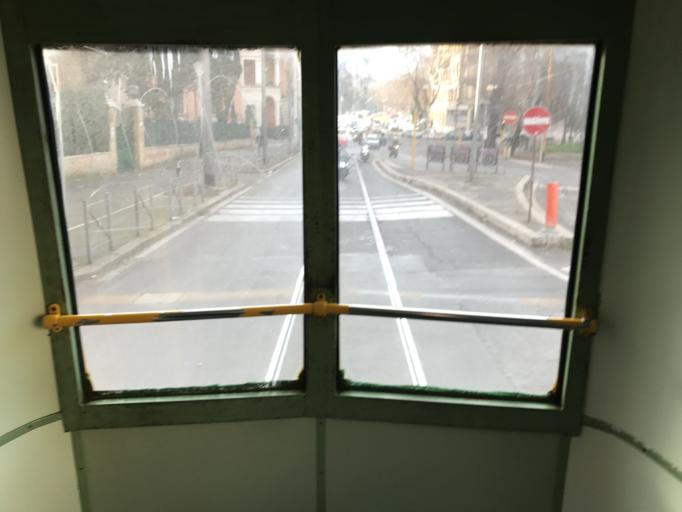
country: VA
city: Vatican City
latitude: 41.9189
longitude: 12.4738
